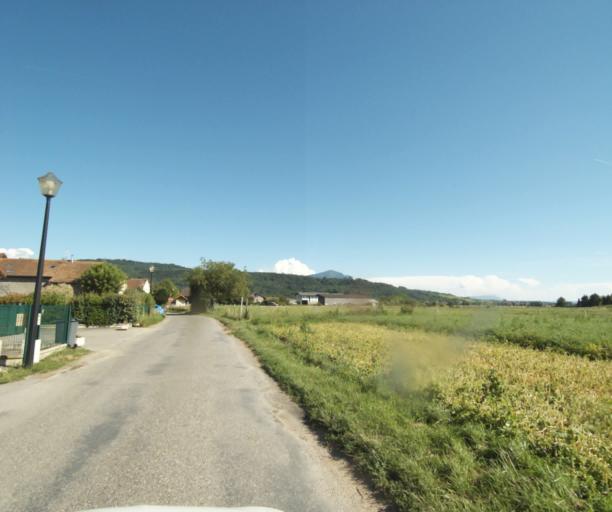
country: FR
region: Rhone-Alpes
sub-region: Departement de la Haute-Savoie
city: Massongy
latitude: 46.3234
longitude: 6.3200
